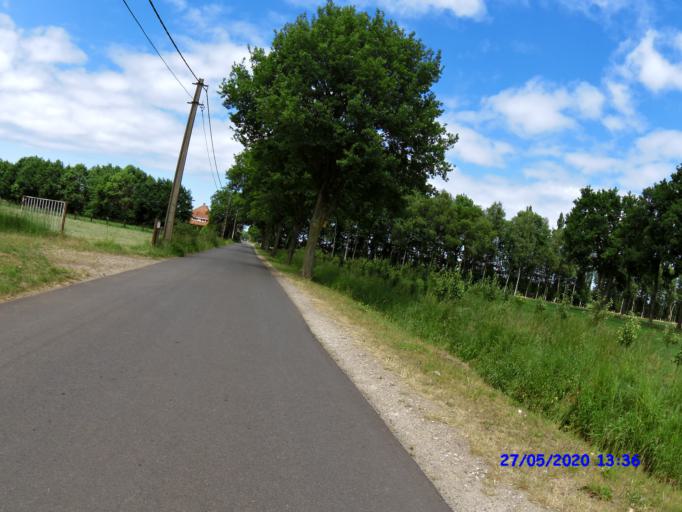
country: BE
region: Flanders
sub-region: Provincie Antwerpen
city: Kasterlee
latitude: 51.2001
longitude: 4.9496
